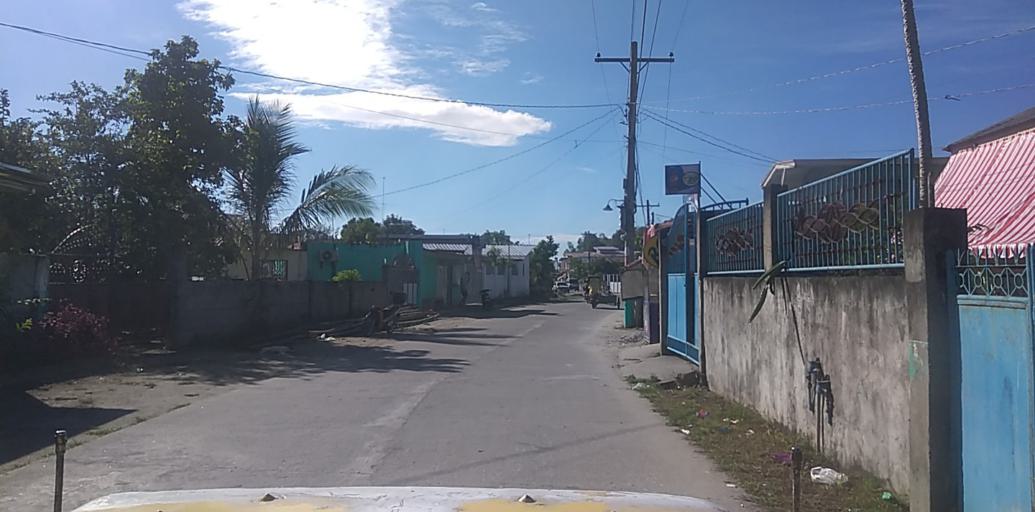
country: PH
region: Central Luzon
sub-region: Province of Pampanga
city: San Patricio
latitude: 15.1115
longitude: 120.7118
